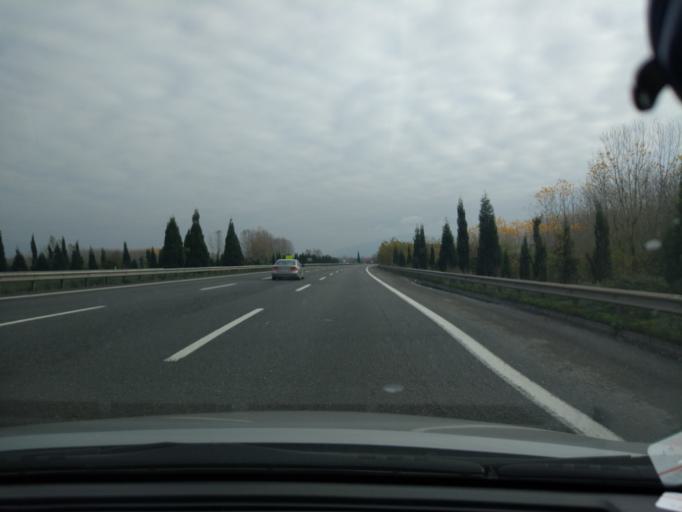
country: TR
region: Sakarya
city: Akyazi
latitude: 40.7418
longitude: 30.6584
